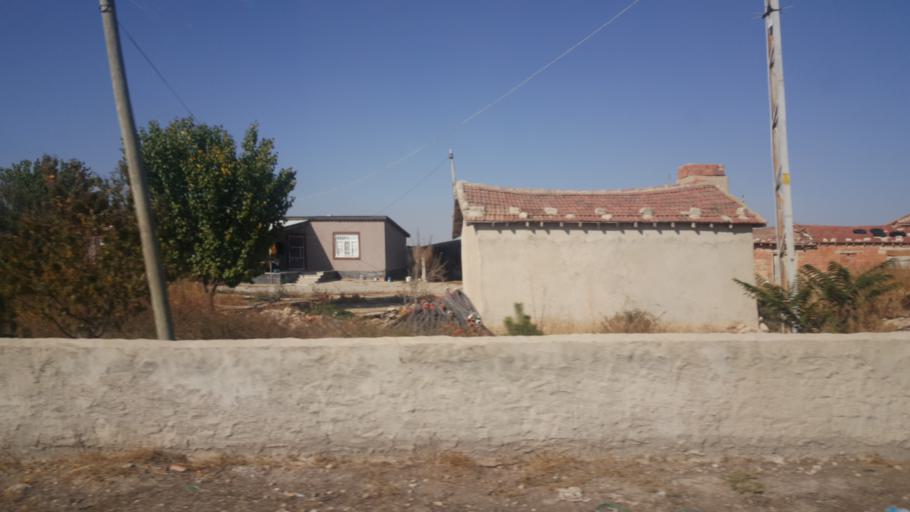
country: TR
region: Konya
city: Celtik
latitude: 39.0591
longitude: 31.8488
